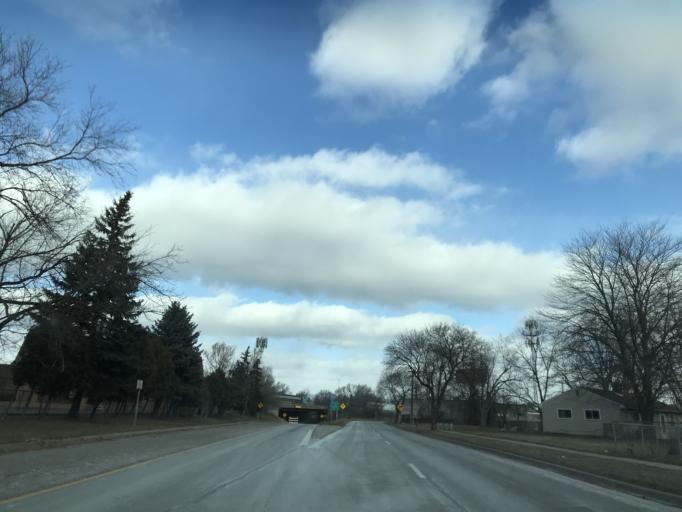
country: US
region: Michigan
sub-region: Oakland County
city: Hazel Park
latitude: 42.4739
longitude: -83.1101
